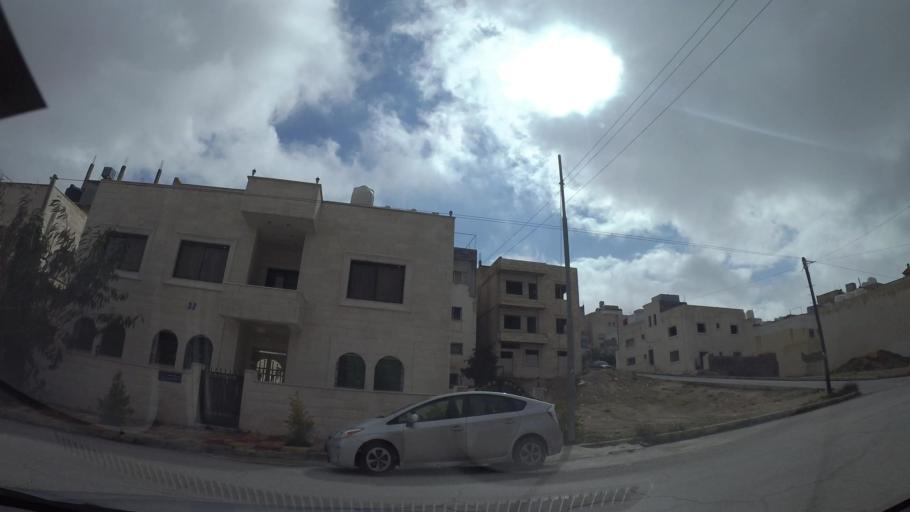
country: JO
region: Amman
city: Al Jubayhah
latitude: 32.0701
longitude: 35.8829
